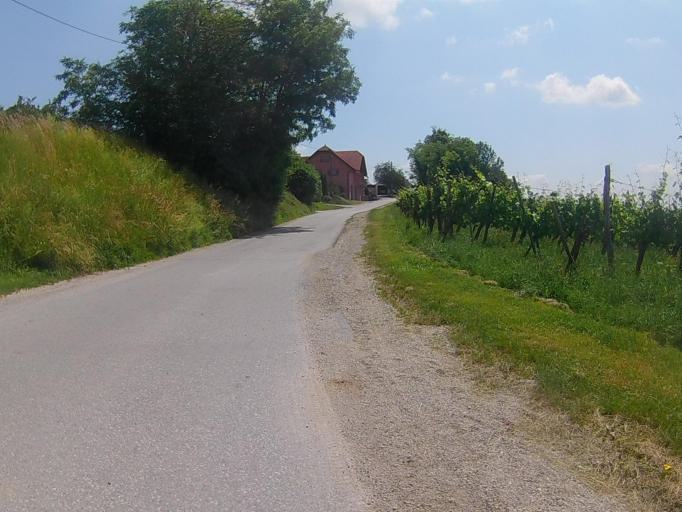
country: SI
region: Pesnica
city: Pesnica pri Mariboru
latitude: 46.5728
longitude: 15.6970
